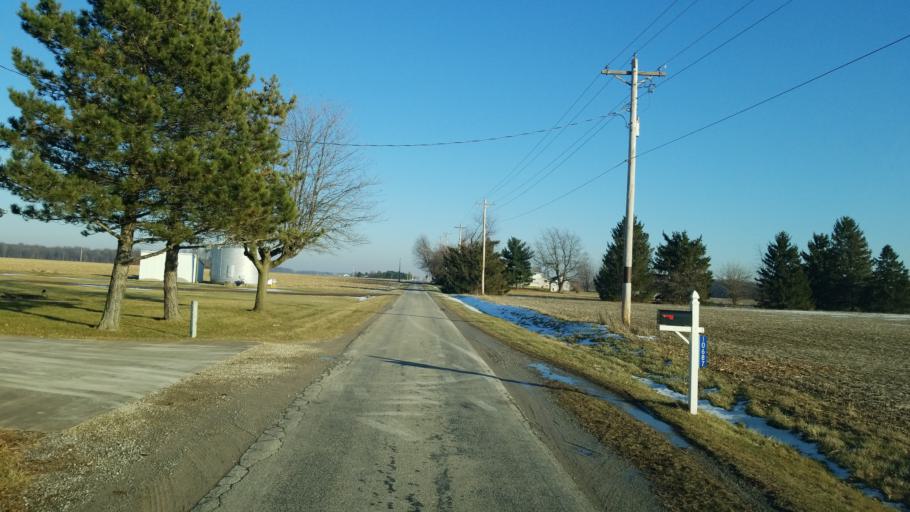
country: US
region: Ohio
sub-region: Crawford County
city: Bucyrus
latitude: 41.0082
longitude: -82.9649
